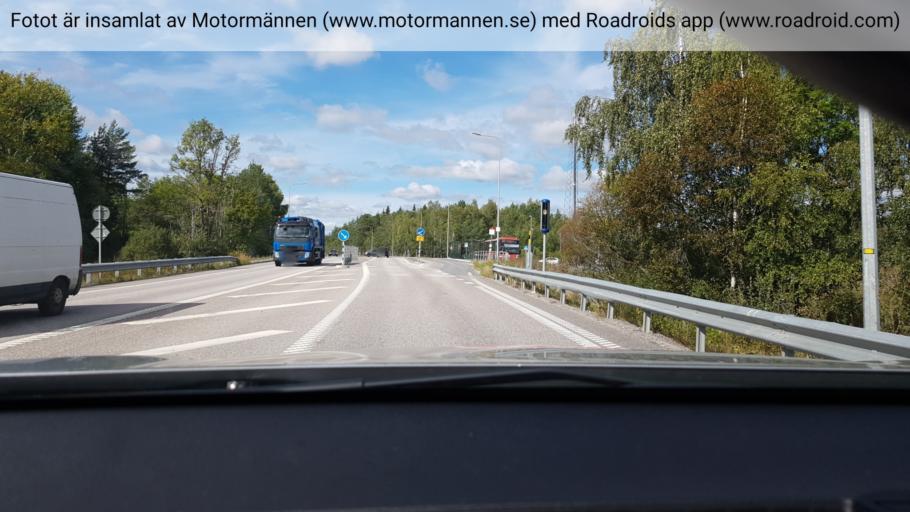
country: SE
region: Stockholm
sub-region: Osterakers Kommun
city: Akersberga
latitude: 59.4490
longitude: 18.2181
